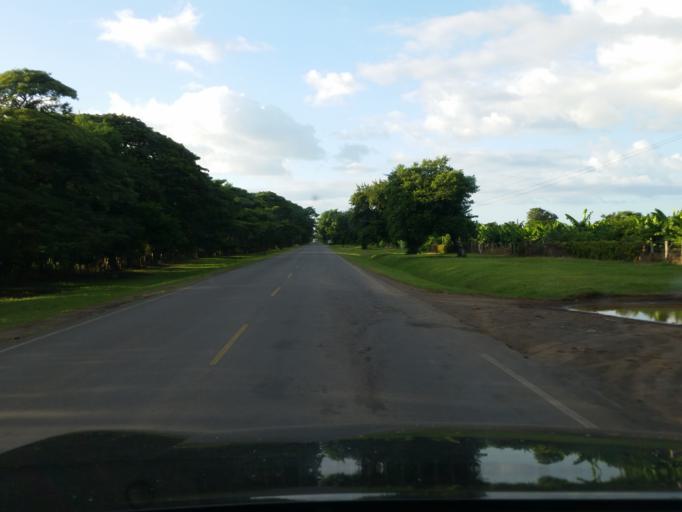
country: NI
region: Granada
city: Nandaime
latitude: 11.7378
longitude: -86.0205
